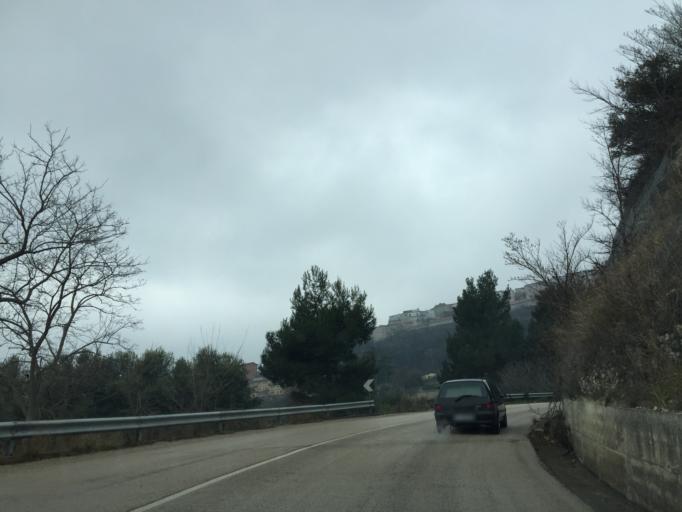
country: IT
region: Apulia
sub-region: Provincia di Foggia
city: Bovino
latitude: 41.2526
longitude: 15.3483
